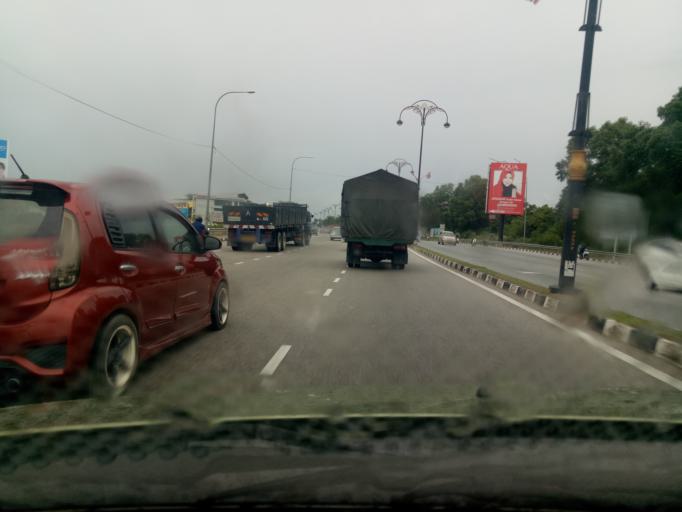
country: MY
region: Kedah
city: Sungai Petani
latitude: 5.6762
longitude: 100.5078
